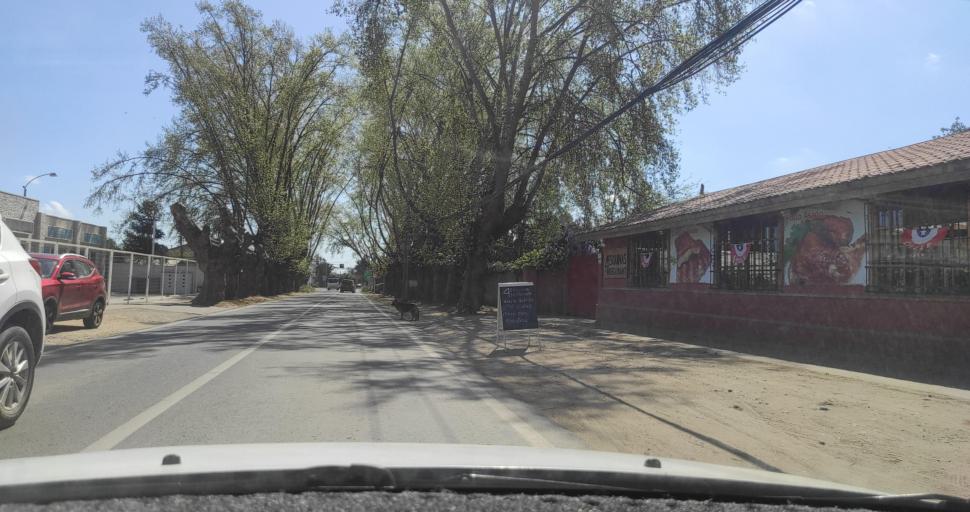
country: CL
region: Valparaiso
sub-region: Provincia de Marga Marga
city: Limache
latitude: -33.0092
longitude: -71.2487
